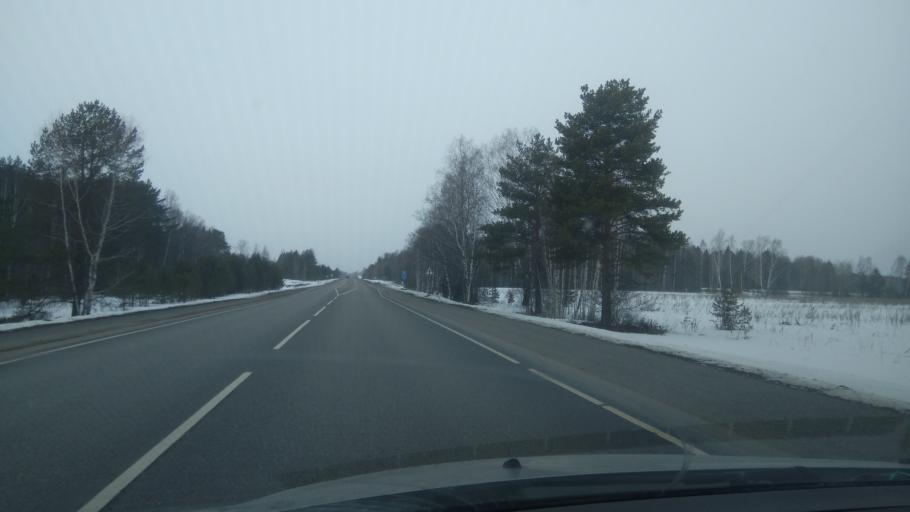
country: RU
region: Perm
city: Suksun
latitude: 56.9169
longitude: 57.5768
